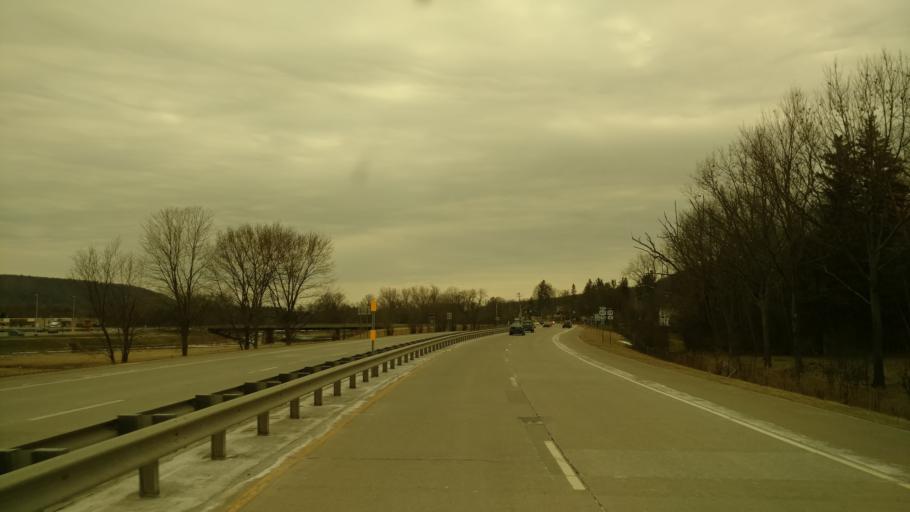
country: US
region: New York
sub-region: Allegany County
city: Wellsville
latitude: 42.1260
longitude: -77.9587
